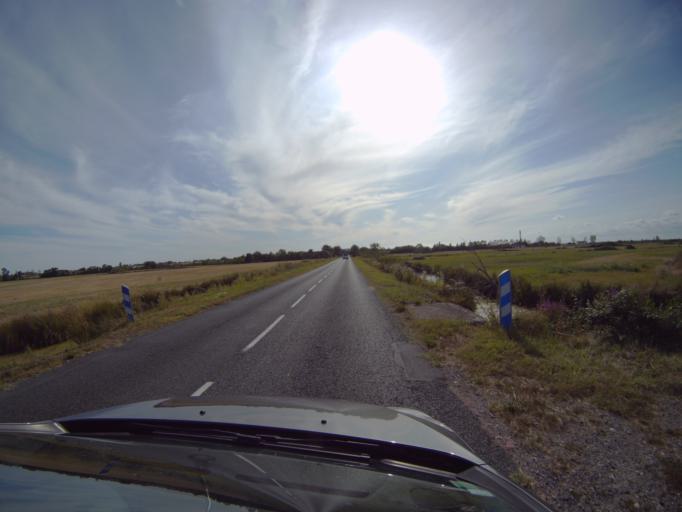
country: FR
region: Pays de la Loire
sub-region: Departement de la Vendee
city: Triaize
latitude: 46.4015
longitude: -1.2911
